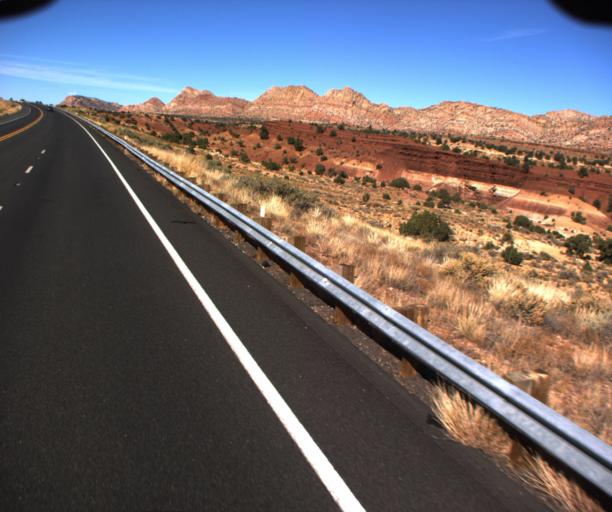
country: US
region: Arizona
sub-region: Coconino County
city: Tuba City
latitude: 36.3572
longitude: -111.5070
